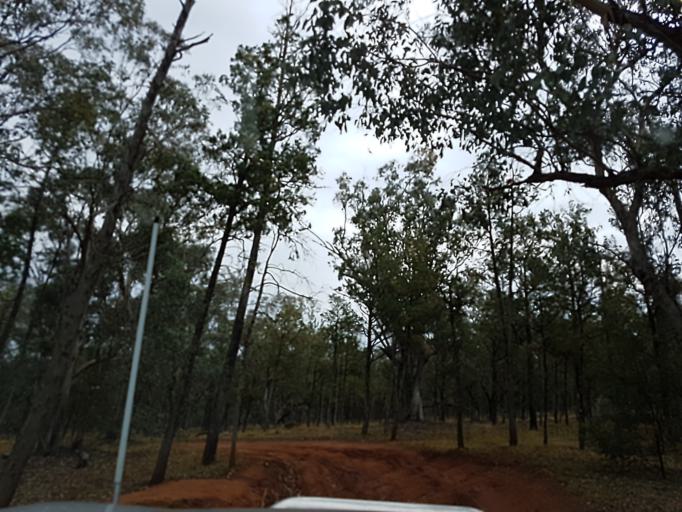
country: AU
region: New South Wales
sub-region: Snowy River
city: Jindabyne
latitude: -36.9357
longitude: 148.4000
